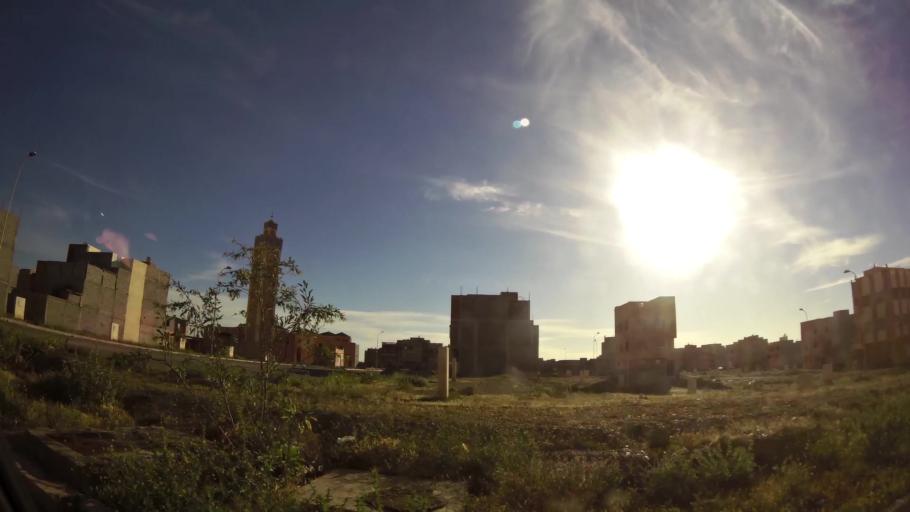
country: MA
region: Marrakech-Tensift-Al Haouz
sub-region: Marrakech
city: Marrakesh
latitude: 31.7586
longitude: -8.0981
